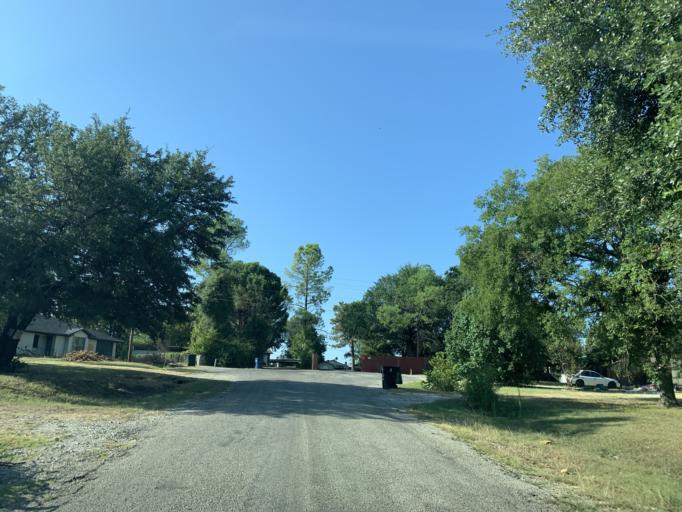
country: US
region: Texas
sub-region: Tarrant County
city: Lakeside
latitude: 32.8543
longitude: -97.5139
